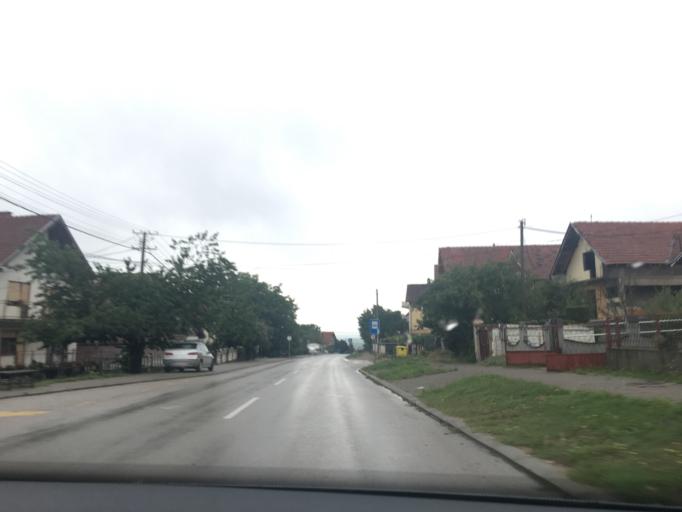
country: RS
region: Central Serbia
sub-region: Nisavski Okrug
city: Aleksinac
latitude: 43.5456
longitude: 21.6957
